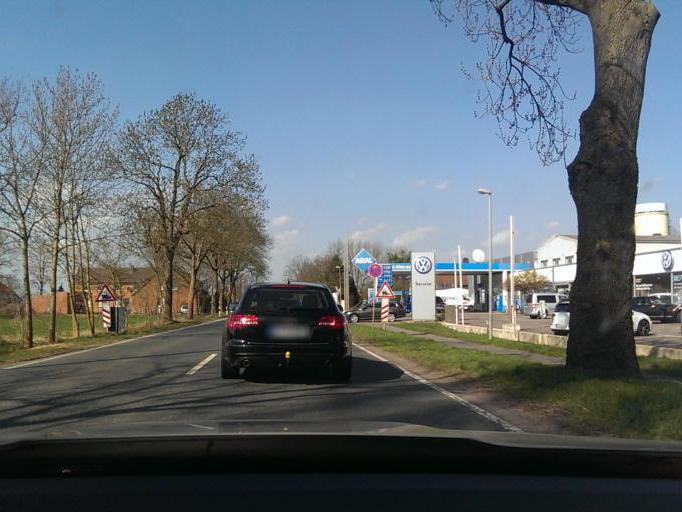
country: DE
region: Lower Saxony
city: Elze
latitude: 52.5766
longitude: 9.7278
